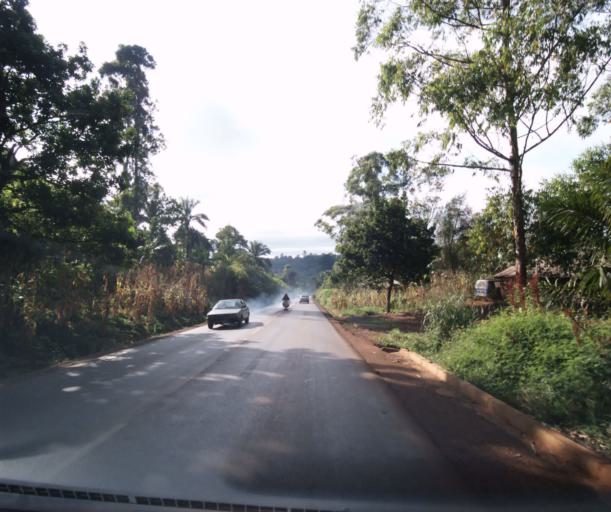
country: CM
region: West
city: Mbouda
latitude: 5.6063
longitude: 10.2914
